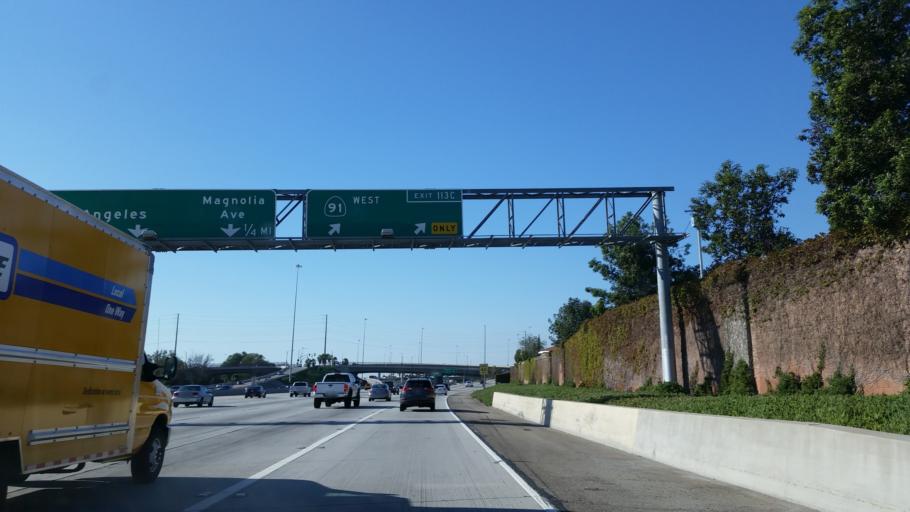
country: US
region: California
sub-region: Orange County
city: Buena Park
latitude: 33.8524
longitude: -117.9718
